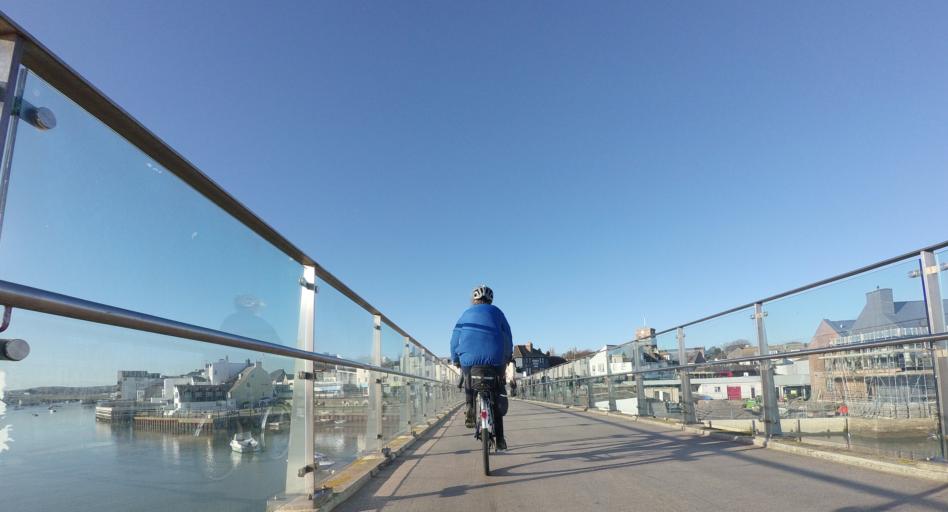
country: GB
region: England
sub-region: West Sussex
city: Shoreham-by-Sea
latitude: 50.8310
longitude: -0.2742
